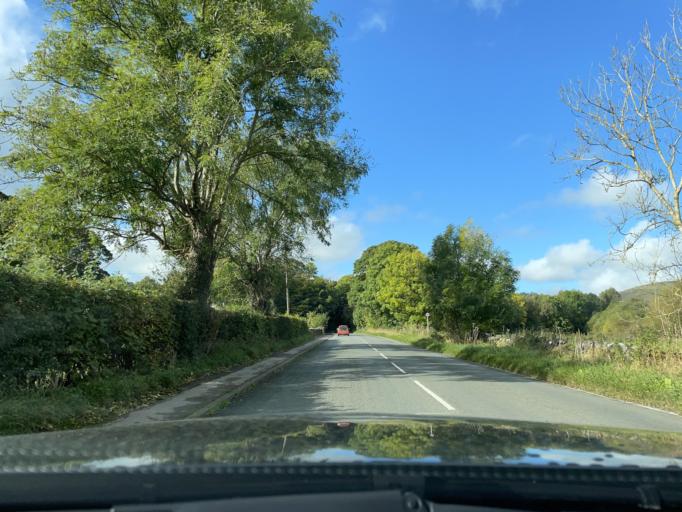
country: GB
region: England
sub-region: Derbyshire
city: Hope Valley
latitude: 53.3474
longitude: -1.7628
